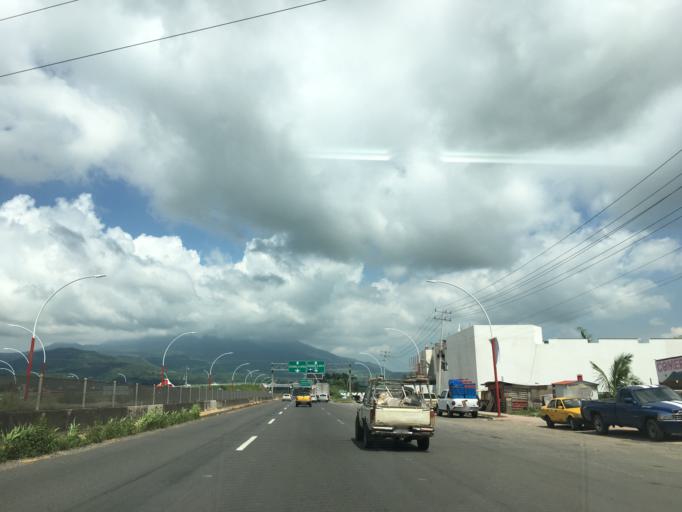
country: MX
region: Nayarit
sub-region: Tepic
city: La Corregidora
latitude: 21.4660
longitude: -104.8361
